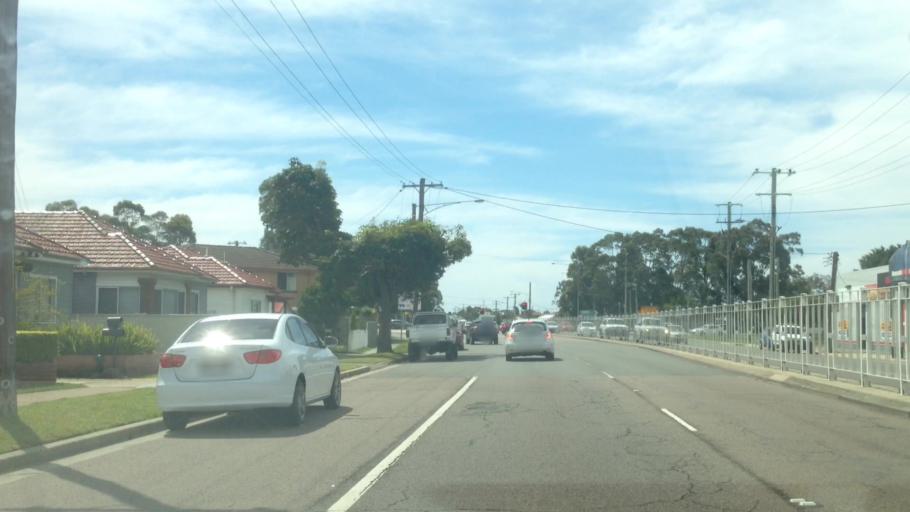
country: AU
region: New South Wales
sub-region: Newcastle
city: Broadmeadow
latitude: -32.9166
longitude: 151.7252
